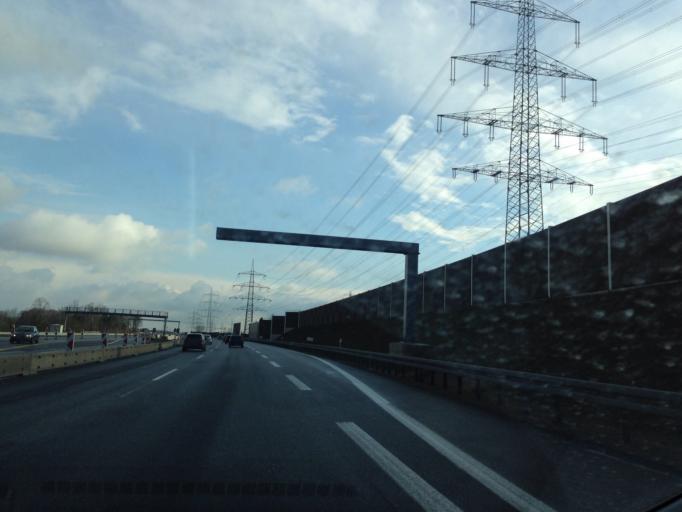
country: DE
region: North Rhine-Westphalia
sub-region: Regierungsbezirk Dusseldorf
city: Kaarst
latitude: 51.2221
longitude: 6.6398
